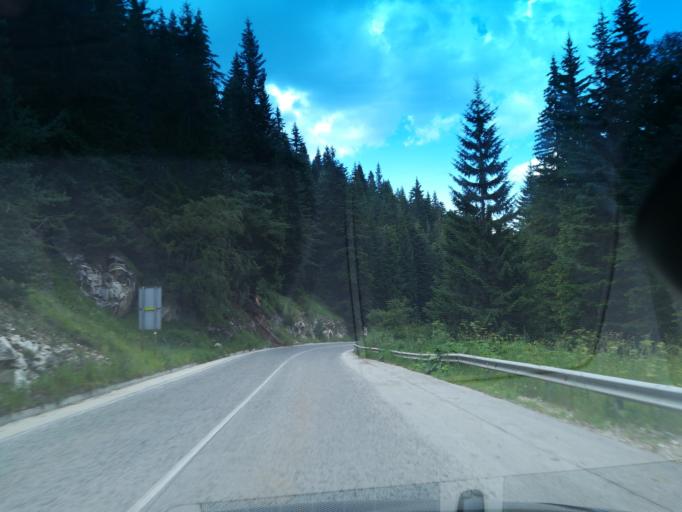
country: BG
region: Smolyan
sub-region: Obshtina Smolyan
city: Smolyan
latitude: 41.6563
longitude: 24.6980
